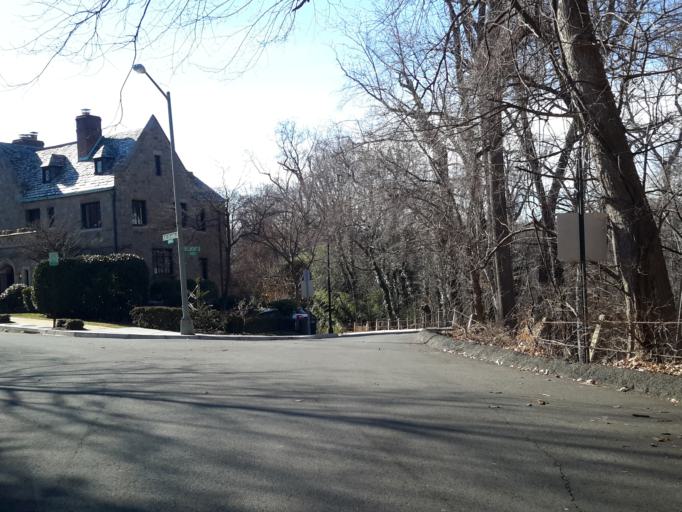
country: US
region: Washington, D.C.
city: Washington, D.C.
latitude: 38.9189
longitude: -77.0527
